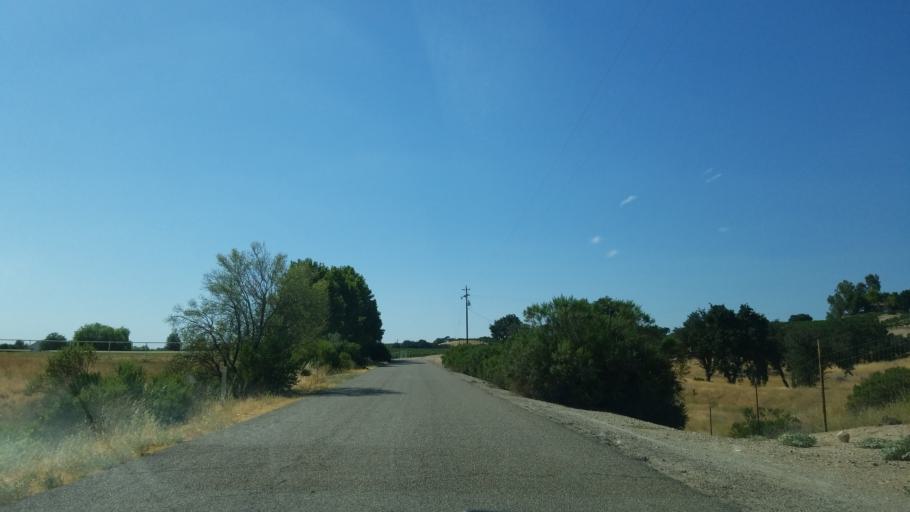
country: US
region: California
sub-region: San Luis Obispo County
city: San Miguel
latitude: 35.7344
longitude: -120.6678
